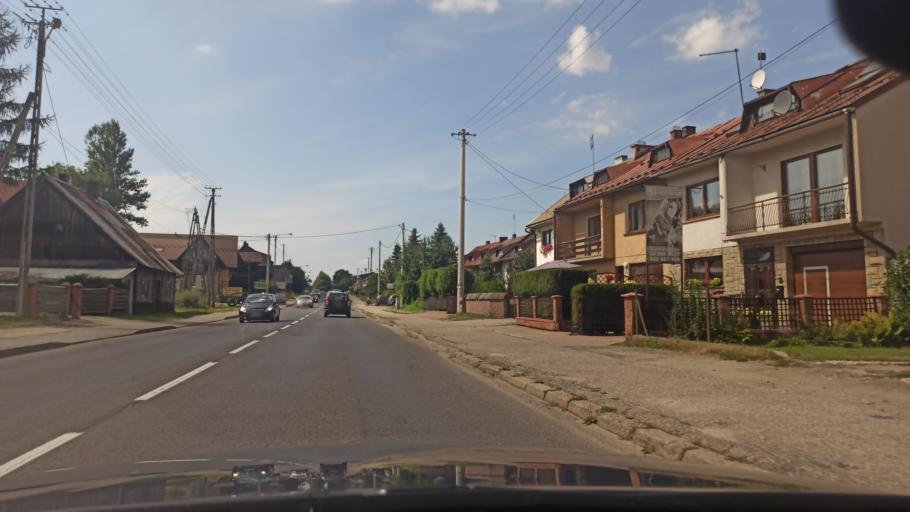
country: PL
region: Lesser Poland Voivodeship
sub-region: Powiat nowotarski
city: Waksmund
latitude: 49.4823
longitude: 20.0720
